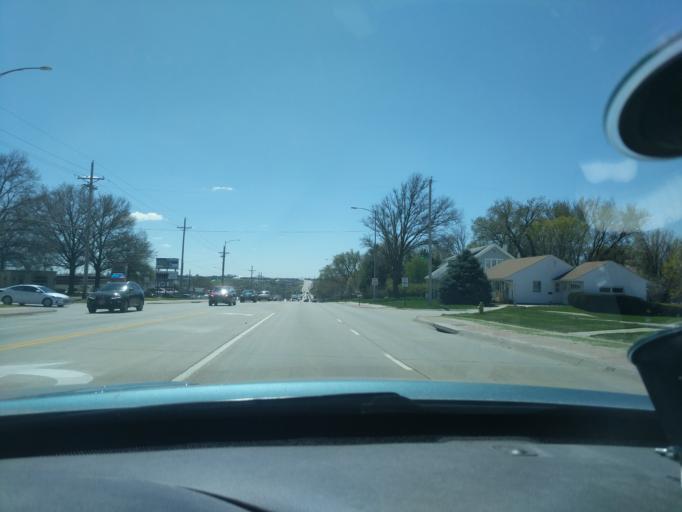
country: US
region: Nebraska
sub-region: Douglas County
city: Elkhorn
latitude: 41.2895
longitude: -96.2344
